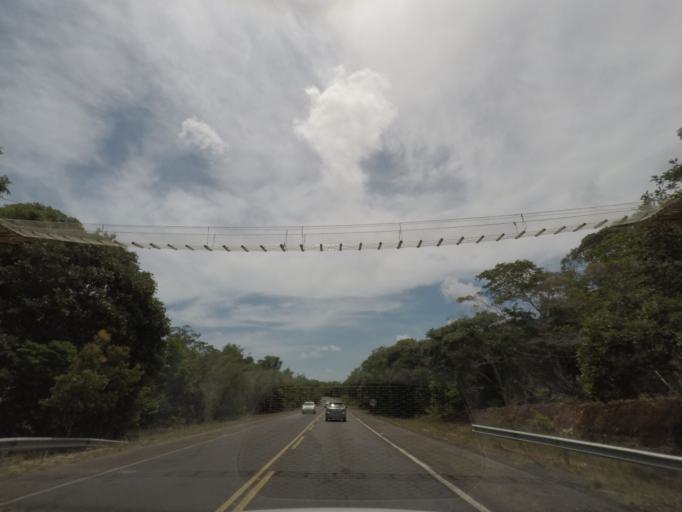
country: BR
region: Bahia
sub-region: Conde
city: Conde
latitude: -12.0367
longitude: -37.7044
